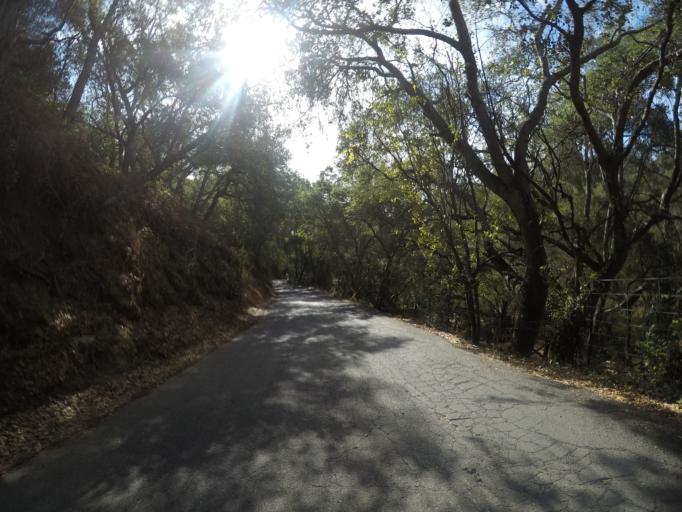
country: US
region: California
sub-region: Santa Cruz County
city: Soquel
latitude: 37.0363
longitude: -121.9672
